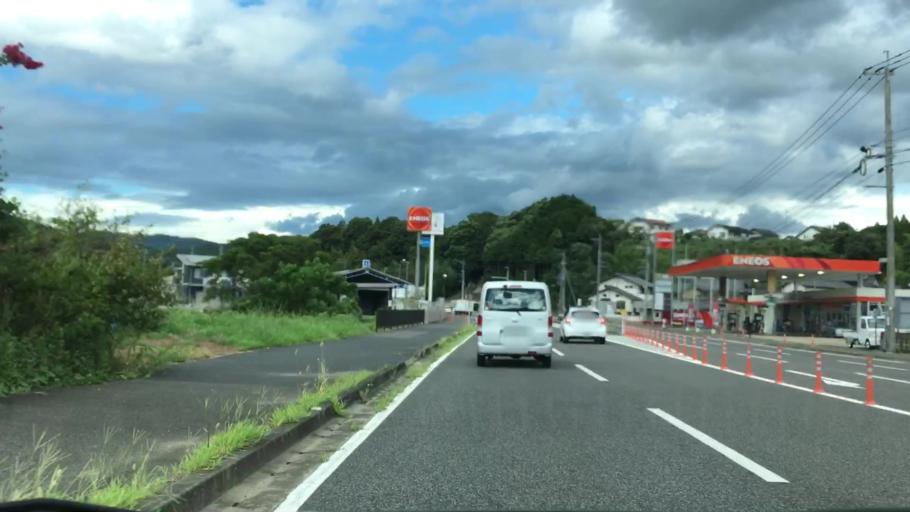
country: JP
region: Saga Prefecture
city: Imaricho-ko
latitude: 33.2758
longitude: 129.8935
